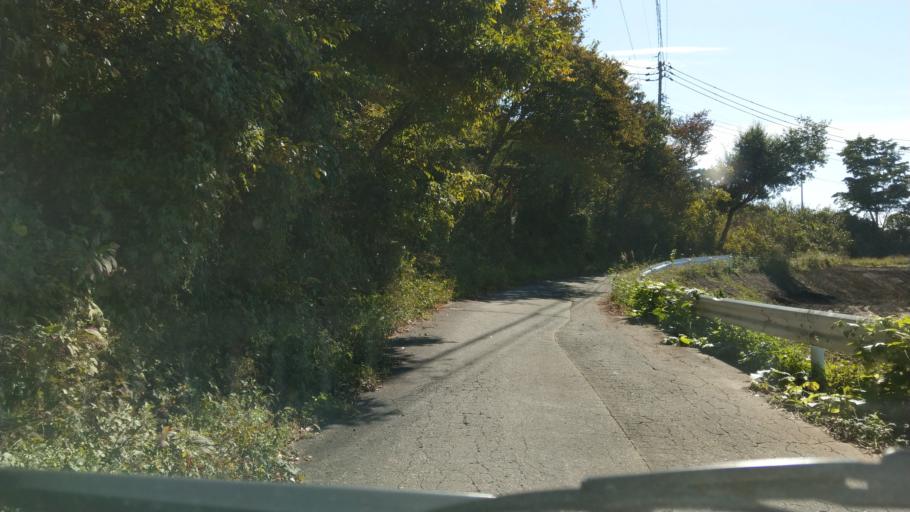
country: JP
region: Nagano
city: Komoro
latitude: 36.3539
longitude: 138.4046
